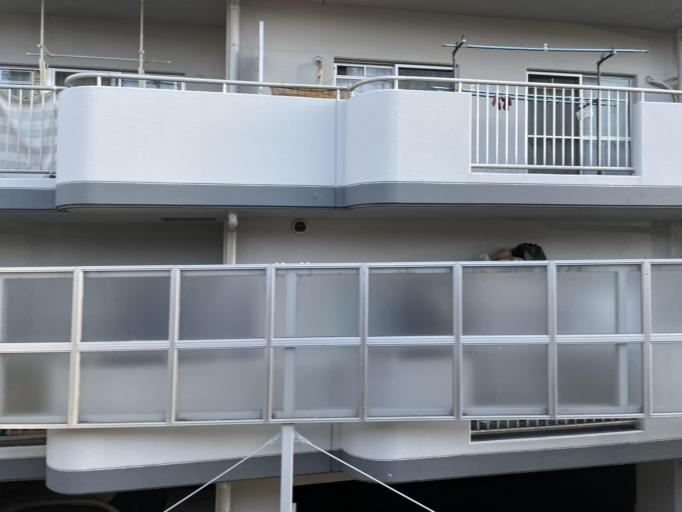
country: JP
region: Osaka
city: Kashihara
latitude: 34.5714
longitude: 135.5974
